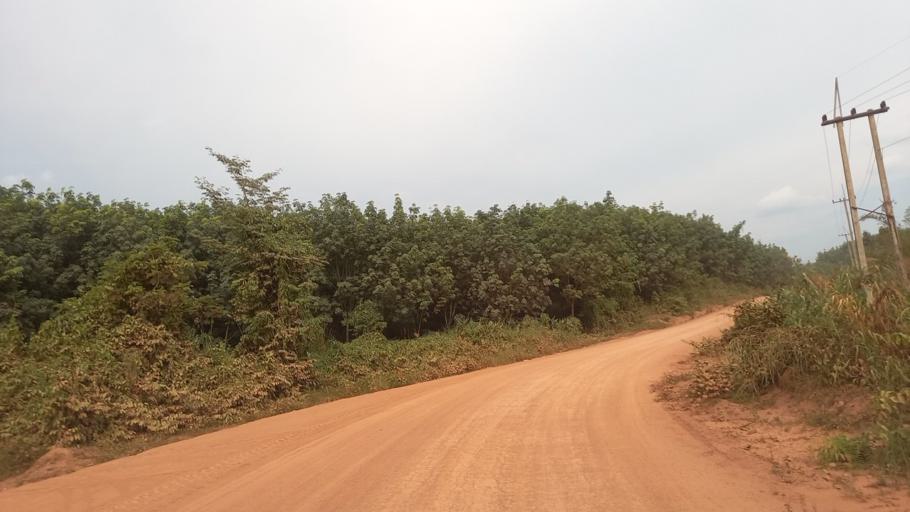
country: LA
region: Bolikhamxai
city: Bolikhan
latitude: 18.5310
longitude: 103.8198
